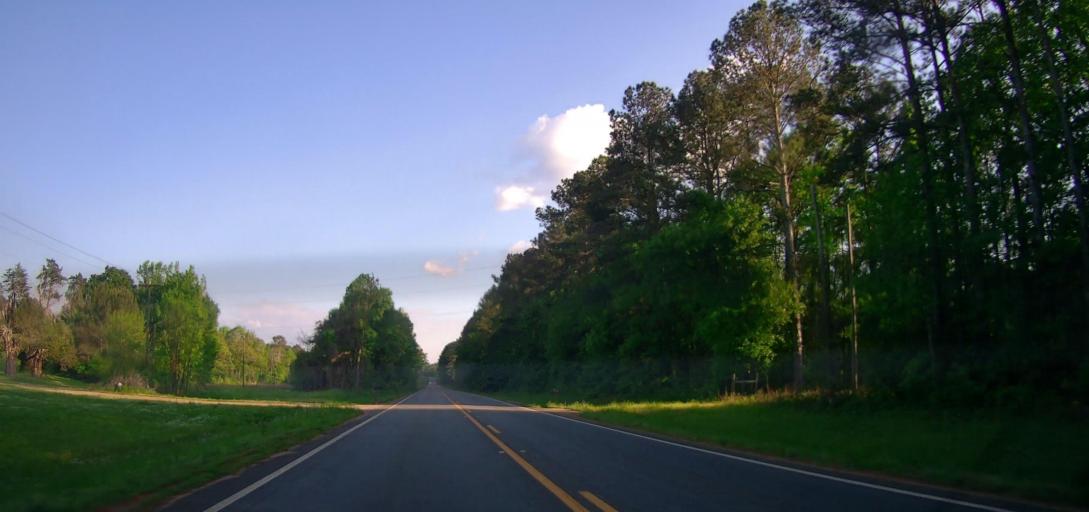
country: US
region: Georgia
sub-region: Putnam County
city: Eatonton
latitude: 33.3484
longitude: -83.5145
